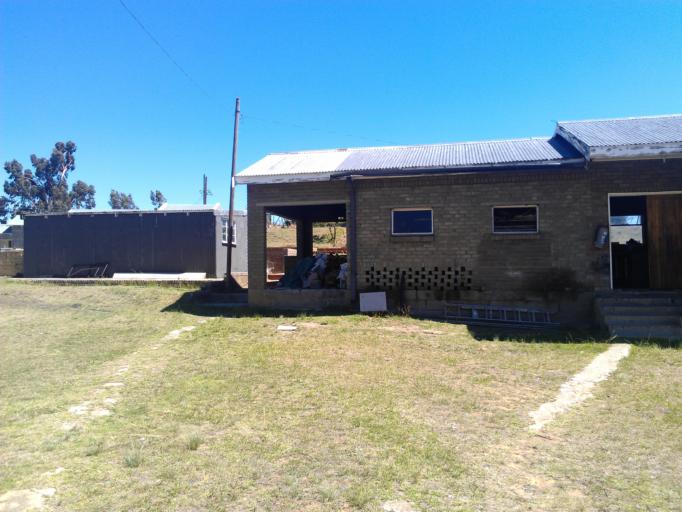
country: LS
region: Qacha's Nek
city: Qacha's Nek
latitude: -30.1029
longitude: 28.6709
